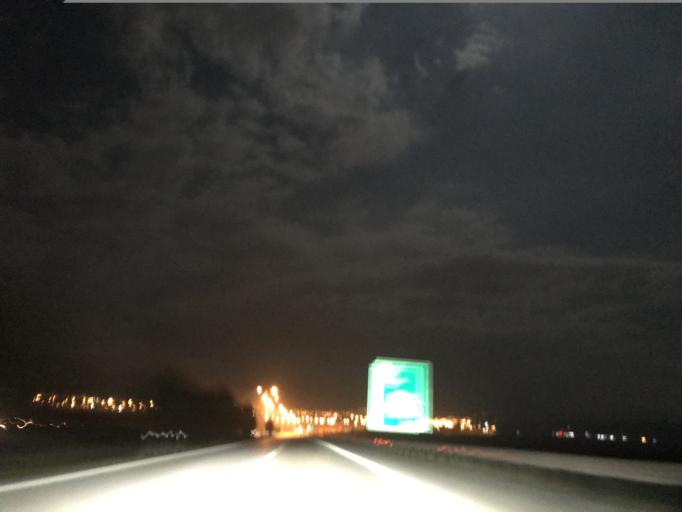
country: TR
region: Hatay
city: Mahmutlar
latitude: 36.9649
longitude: 36.0993
